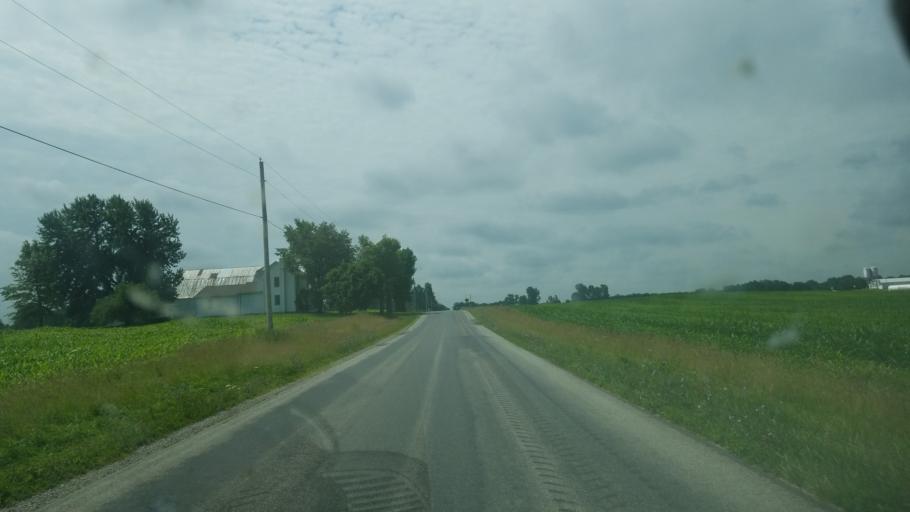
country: US
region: Ohio
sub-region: Licking County
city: Johnstown
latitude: 40.1590
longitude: -82.7594
